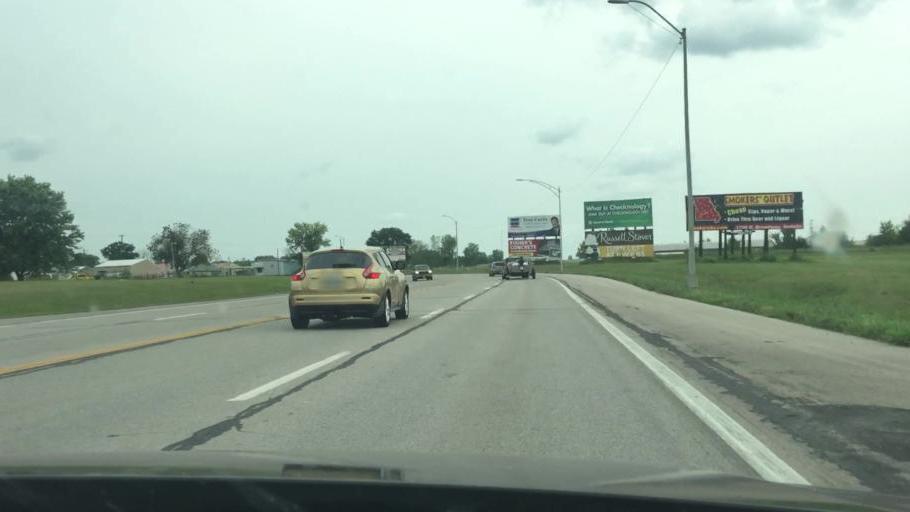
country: US
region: Missouri
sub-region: Pettis County
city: Sedalia
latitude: 38.7045
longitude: -93.1925
